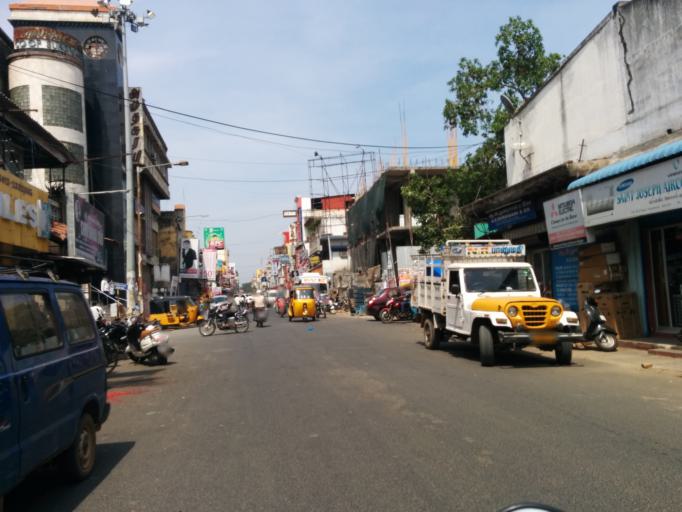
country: IN
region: Pondicherry
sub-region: Puducherry
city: Puducherry
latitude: 11.9338
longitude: 79.8289
